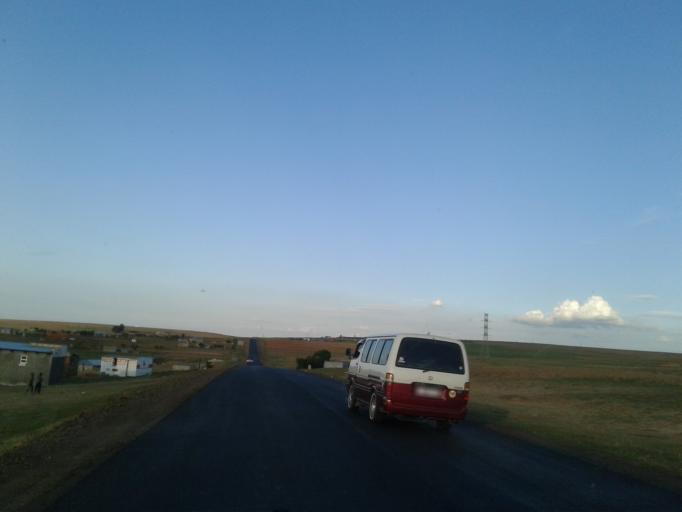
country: LS
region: Maseru
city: Maseru
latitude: -29.3144
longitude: 27.5927
